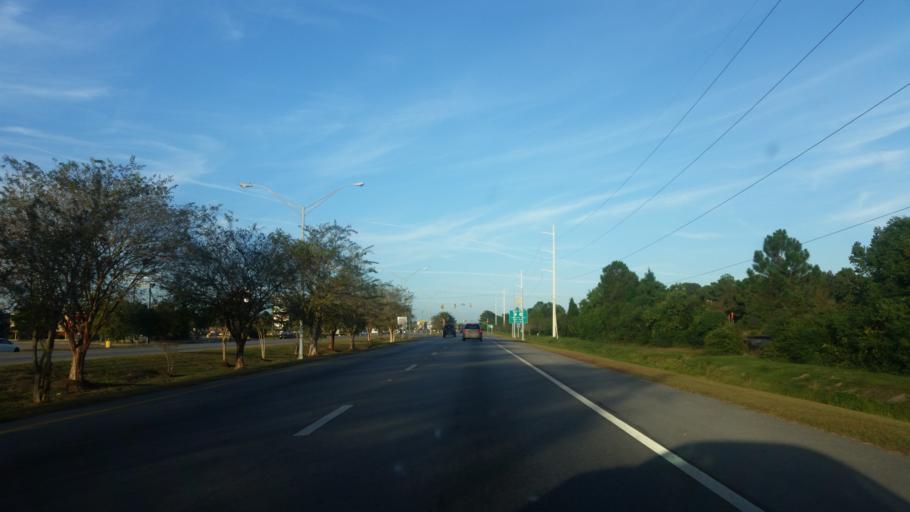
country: US
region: Mississippi
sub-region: Jackson County
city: Moss Point
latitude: 30.3816
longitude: -88.5213
